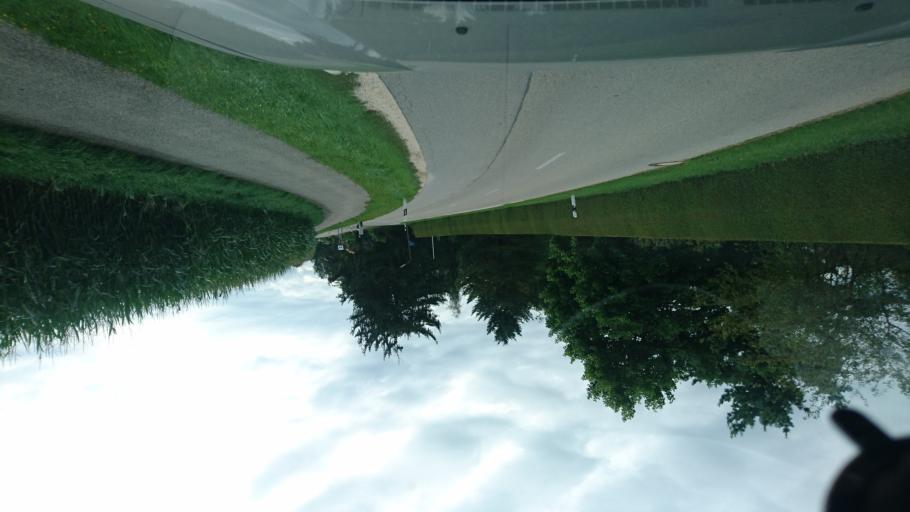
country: DE
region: Bavaria
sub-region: Upper Bavaria
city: Grabenstatt
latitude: 47.8420
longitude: 12.5453
